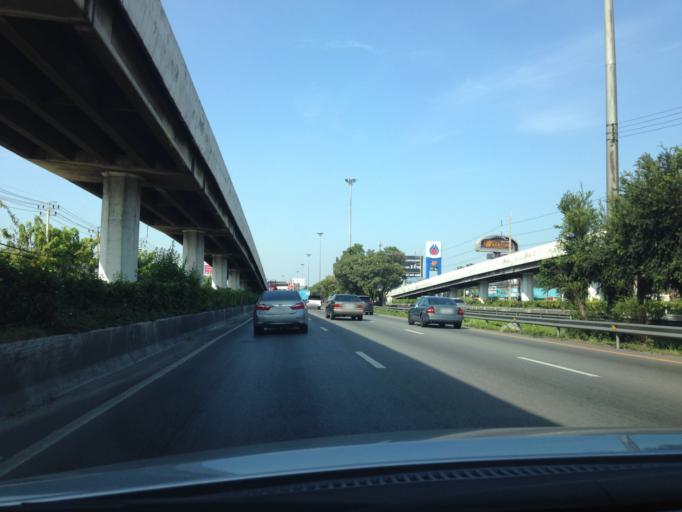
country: TH
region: Nonthaburi
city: Bang Yai
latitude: 13.8305
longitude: 100.4131
